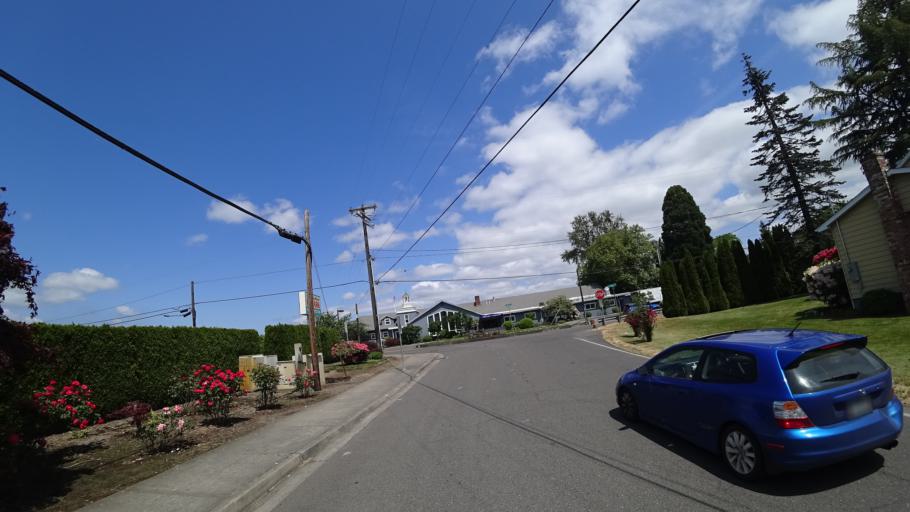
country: US
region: Washington
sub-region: Clark County
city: Vancouver
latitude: 45.6002
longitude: -122.6523
